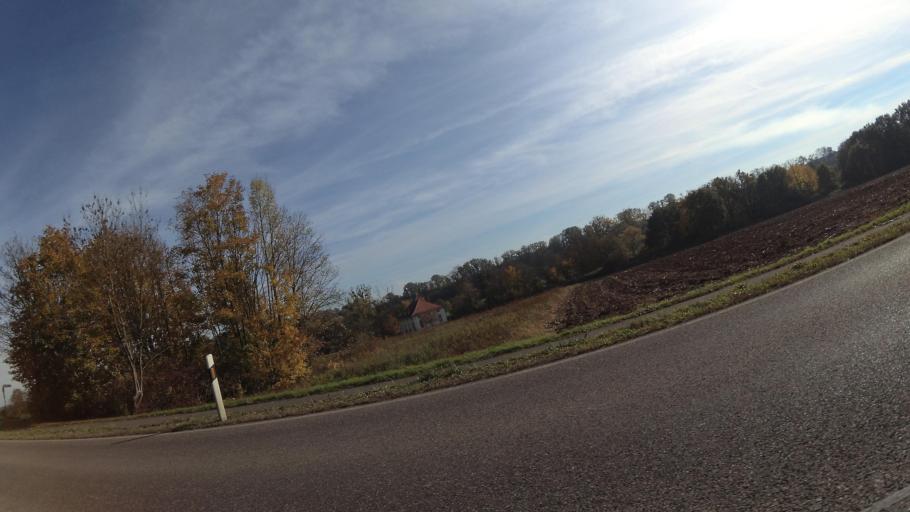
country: DE
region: Baden-Wuerttemberg
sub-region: Regierungsbezirk Stuttgart
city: Offenau
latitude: 49.2458
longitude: 9.1916
